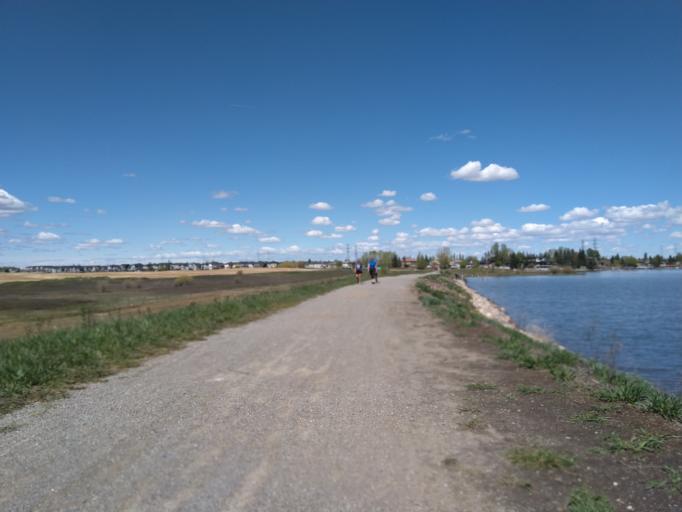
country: CA
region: Alberta
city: Chestermere
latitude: 51.0175
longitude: -113.8234
